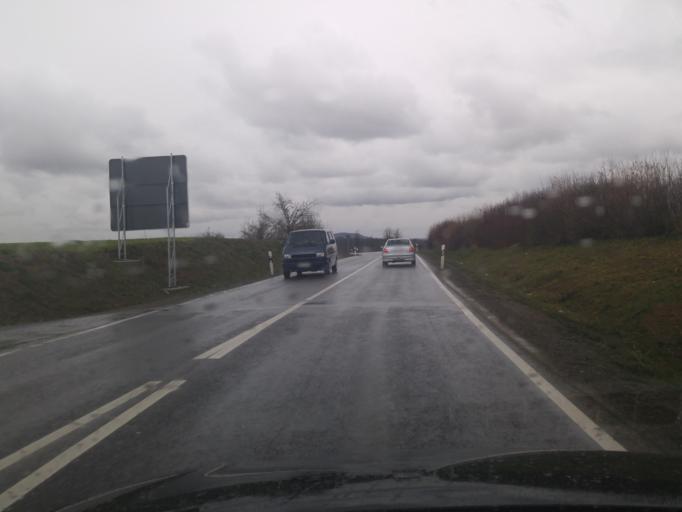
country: DE
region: Baden-Wuerttemberg
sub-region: Regierungsbezirk Stuttgart
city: Affalterbach
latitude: 48.9162
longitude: 9.3332
